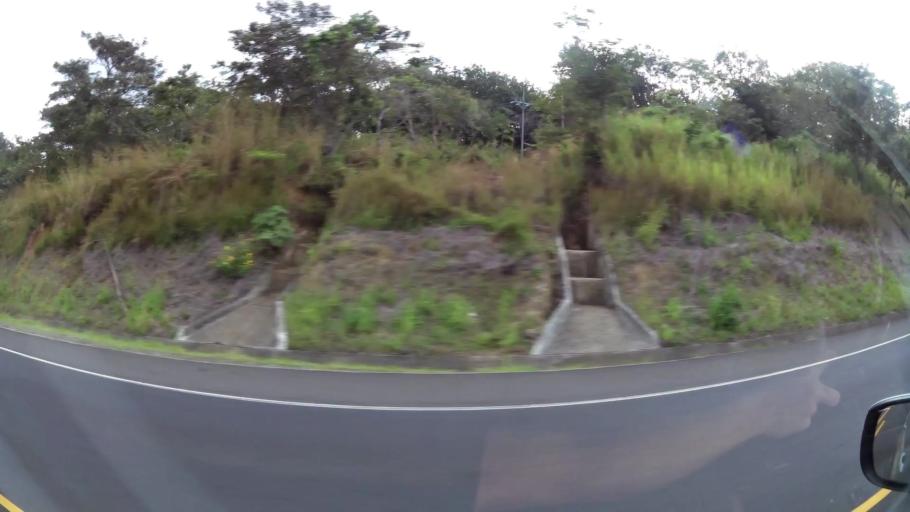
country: CR
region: Alajuela
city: Atenas
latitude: 9.9471
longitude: -84.3645
